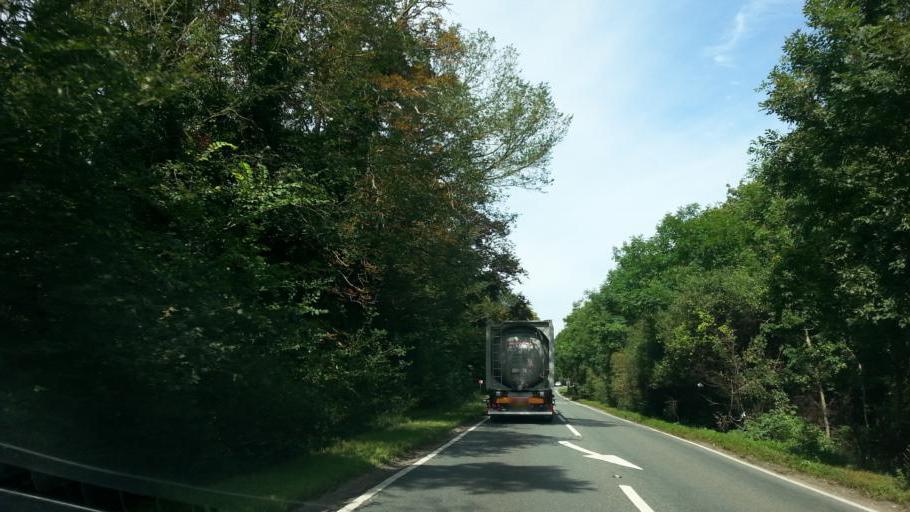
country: GB
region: England
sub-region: Suffolk
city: Exning
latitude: 52.2789
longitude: 0.3941
